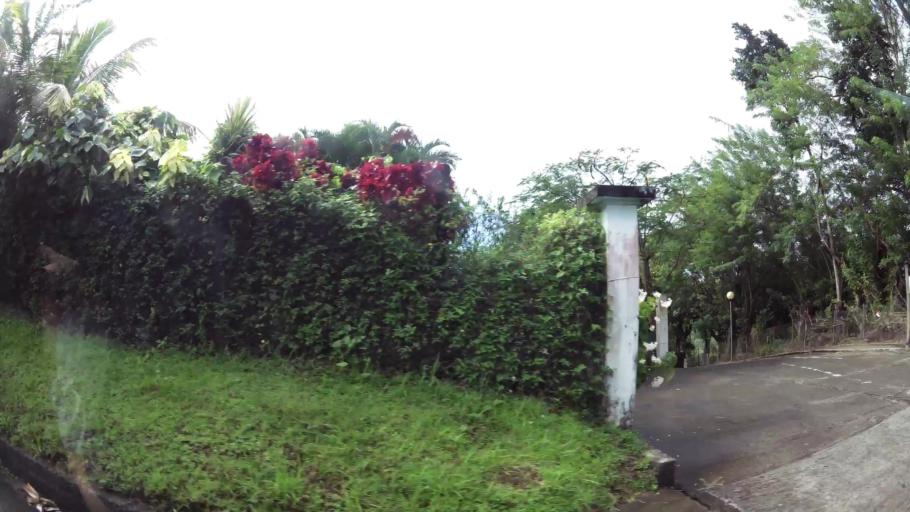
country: MQ
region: Martinique
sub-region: Martinique
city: Saint-Joseph
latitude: 14.6423
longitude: -61.0428
